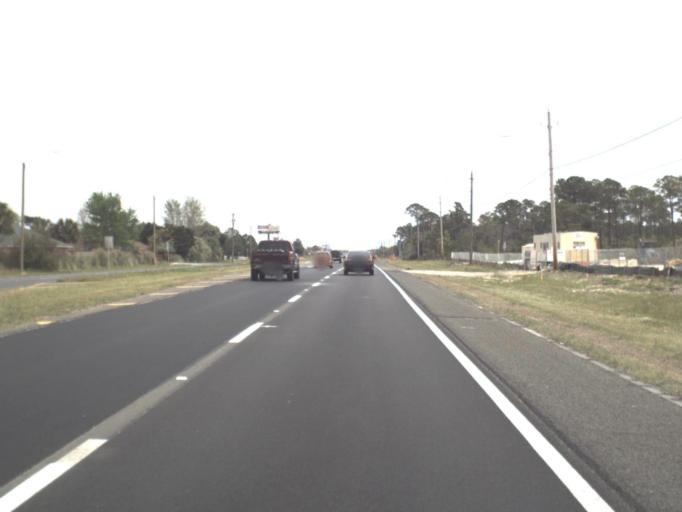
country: US
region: Florida
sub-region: Santa Rosa County
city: Holley
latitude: 30.4019
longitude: -86.9149
